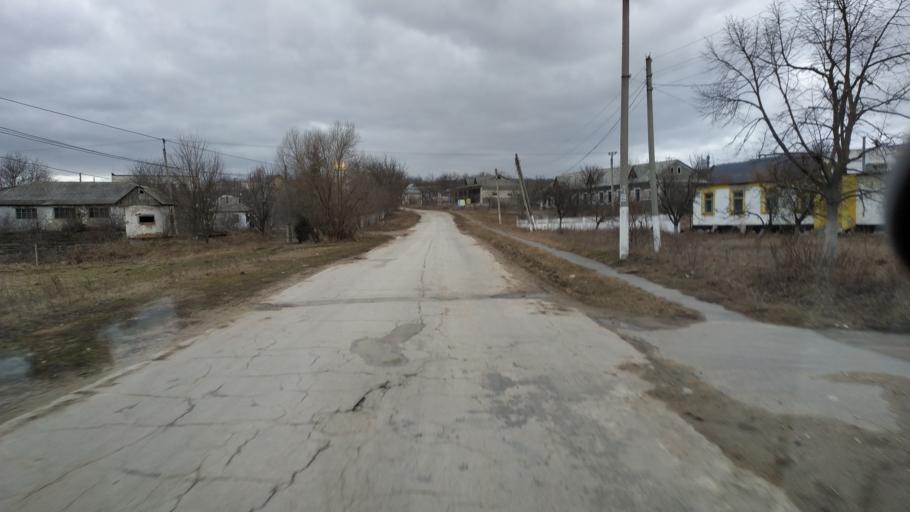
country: MD
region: Calarasi
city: Calarasi
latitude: 47.2561
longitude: 28.1423
